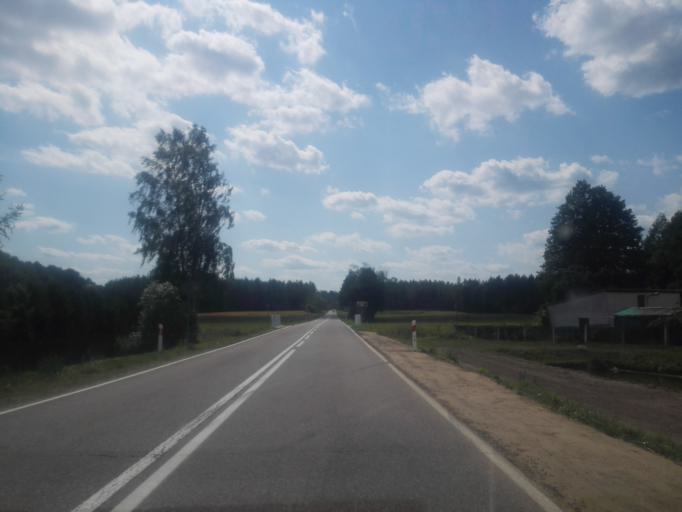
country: PL
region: Podlasie
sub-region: Powiat sejnenski
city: Krasnopol
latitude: 53.9404
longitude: 23.1821
